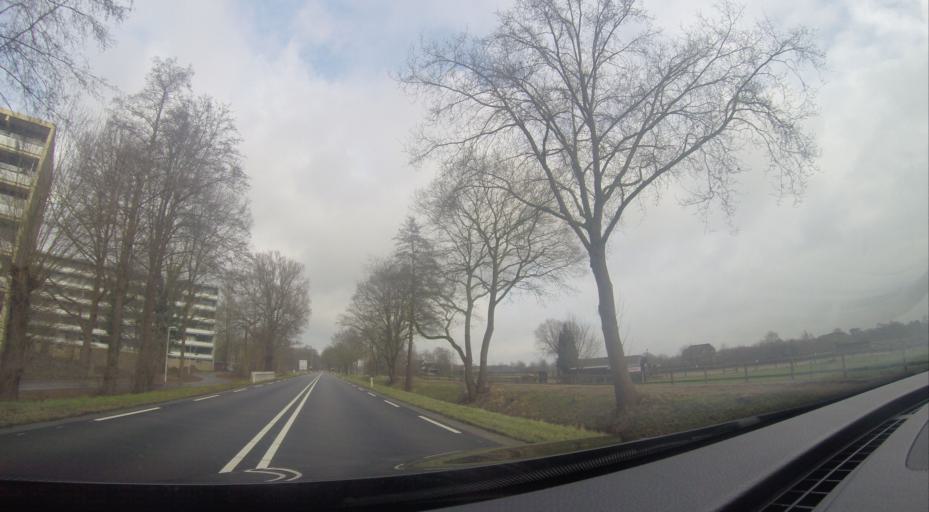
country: NL
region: Gelderland
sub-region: Gemeente Doetinchem
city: Doetinchem
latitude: 51.9741
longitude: 6.3246
